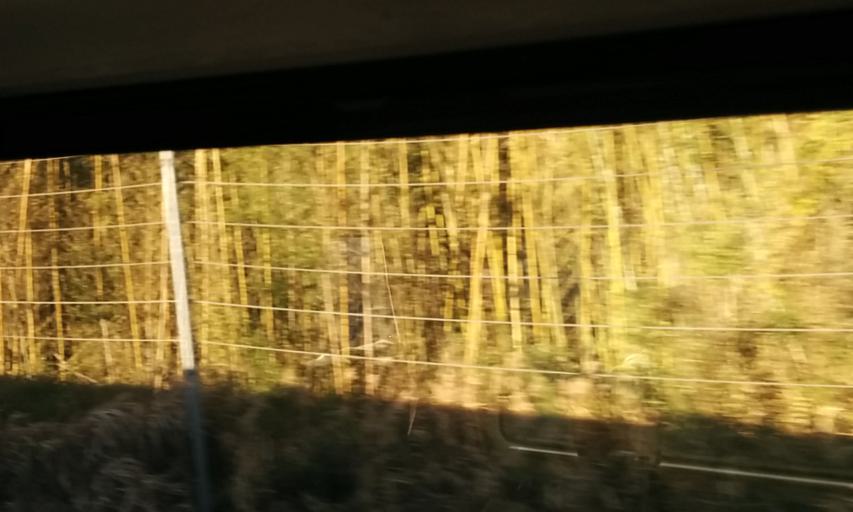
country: JP
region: Gifu
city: Nakatsugawa
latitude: 35.4779
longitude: 137.4605
